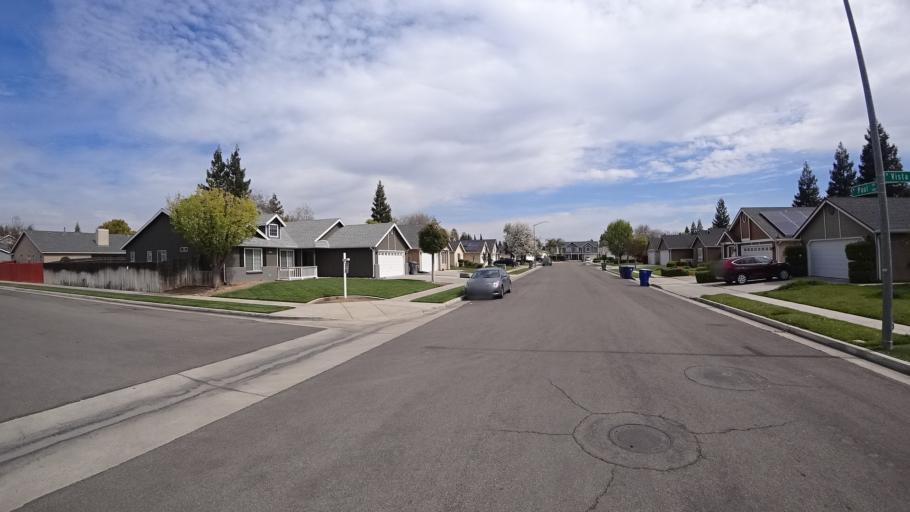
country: US
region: California
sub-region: Fresno County
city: Biola
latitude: 36.8309
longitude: -119.8969
